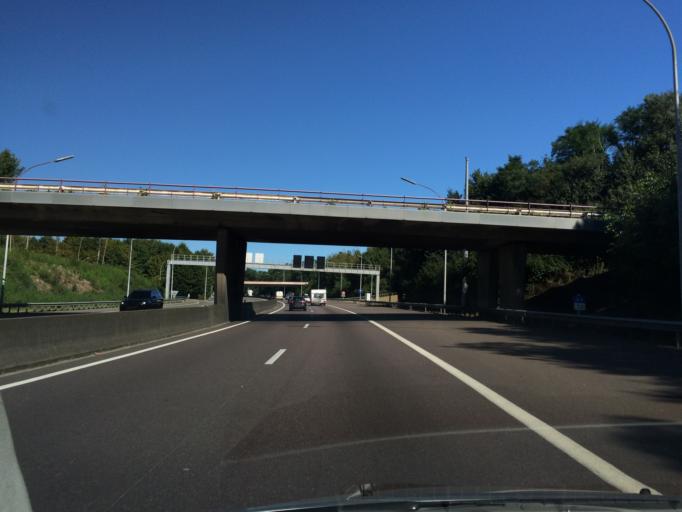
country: LU
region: Luxembourg
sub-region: Canton de Luxembourg
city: Strassen
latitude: 49.6201
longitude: 6.0834
